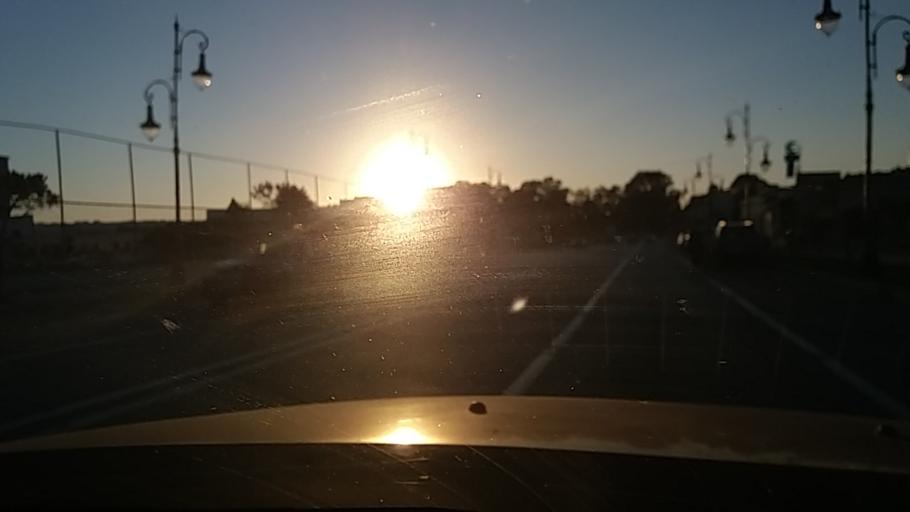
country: MA
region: Tanger-Tetouan
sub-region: Tanger-Assilah
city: Boukhalef
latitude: 35.7401
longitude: -5.8775
